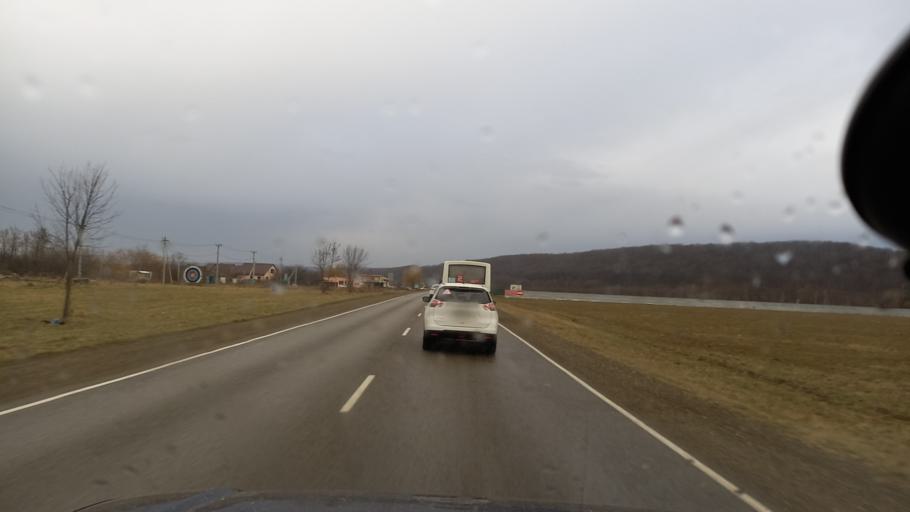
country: RU
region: Adygeya
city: Tul'skiy
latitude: 44.5291
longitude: 40.1369
